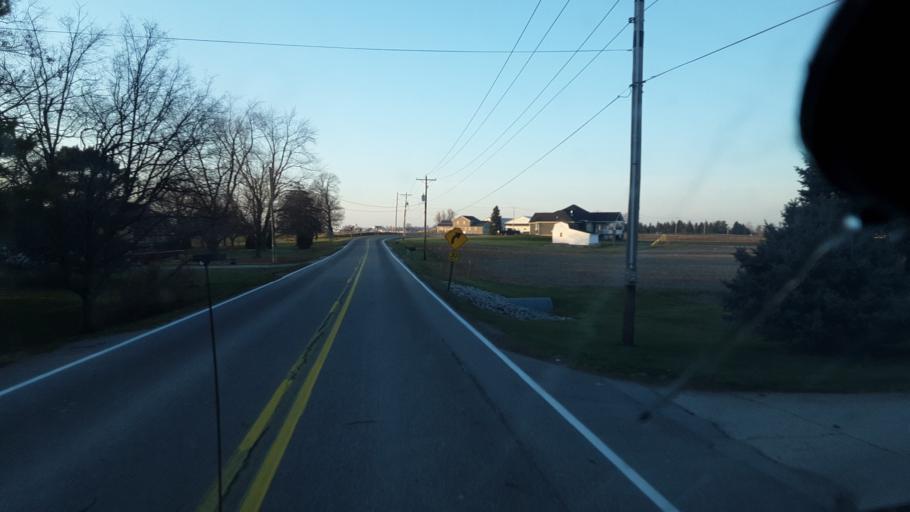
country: US
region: Indiana
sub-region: Allen County
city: Harlan
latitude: 41.1865
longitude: -84.9395
